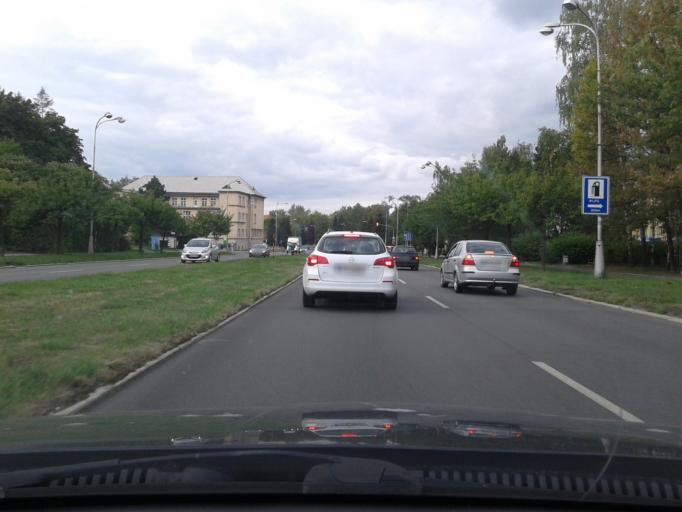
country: CZ
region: Moravskoslezsky
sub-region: Okres Karvina
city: Karvina
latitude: 49.8559
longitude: 18.5477
